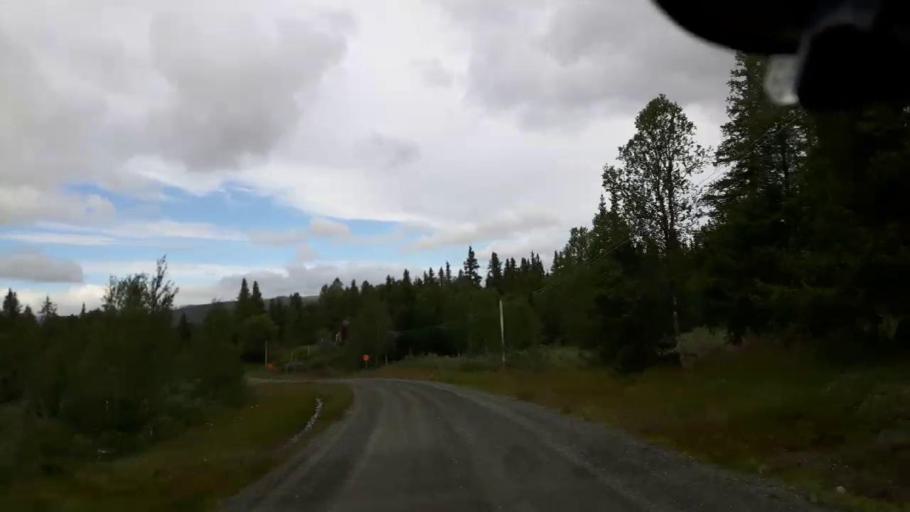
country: SE
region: Jaemtland
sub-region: Krokoms Kommun
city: Valla
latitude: 63.7788
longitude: 13.8293
